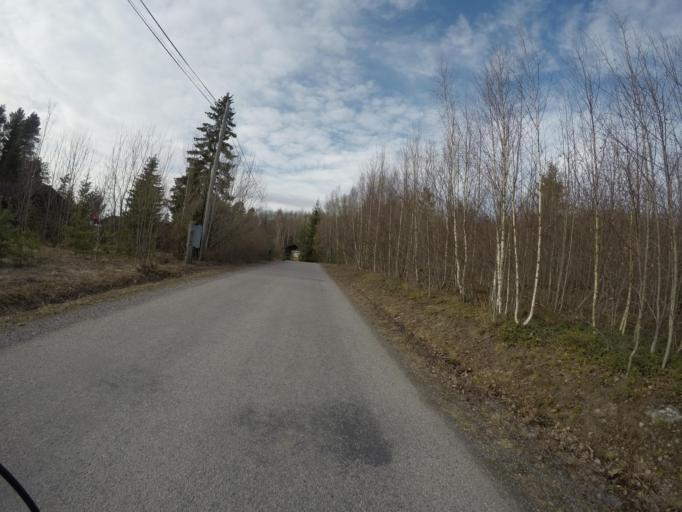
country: SE
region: Soedermanland
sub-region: Eskilstuna Kommun
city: Hallbybrunn
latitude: 59.4344
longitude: 16.4147
